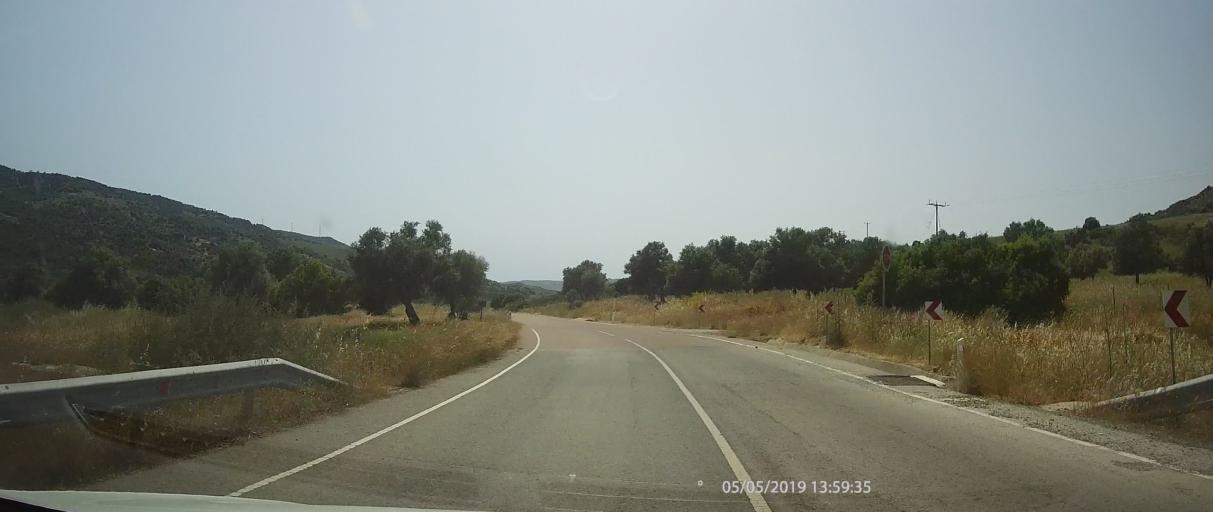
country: CY
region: Limassol
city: Pissouri
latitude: 34.7829
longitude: 32.6760
